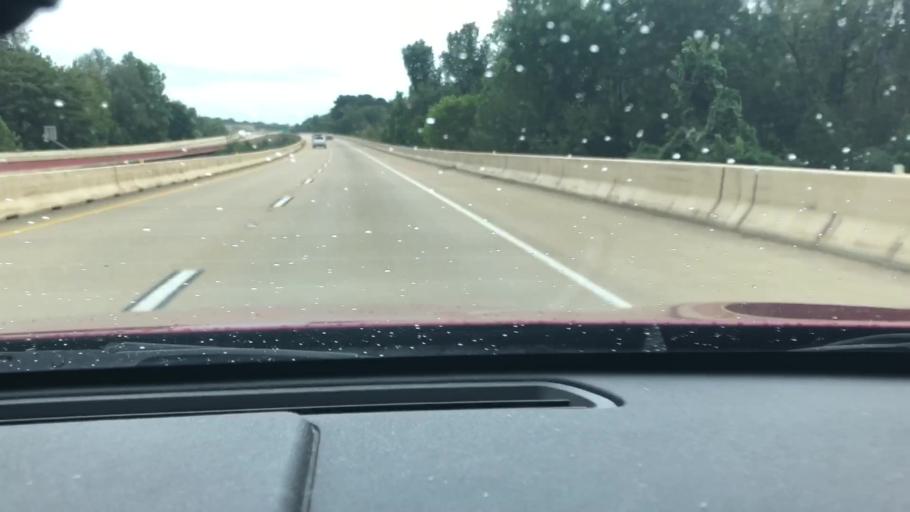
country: US
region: Texas
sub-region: Bowie County
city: Texarkana
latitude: 33.3850
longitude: -94.0564
